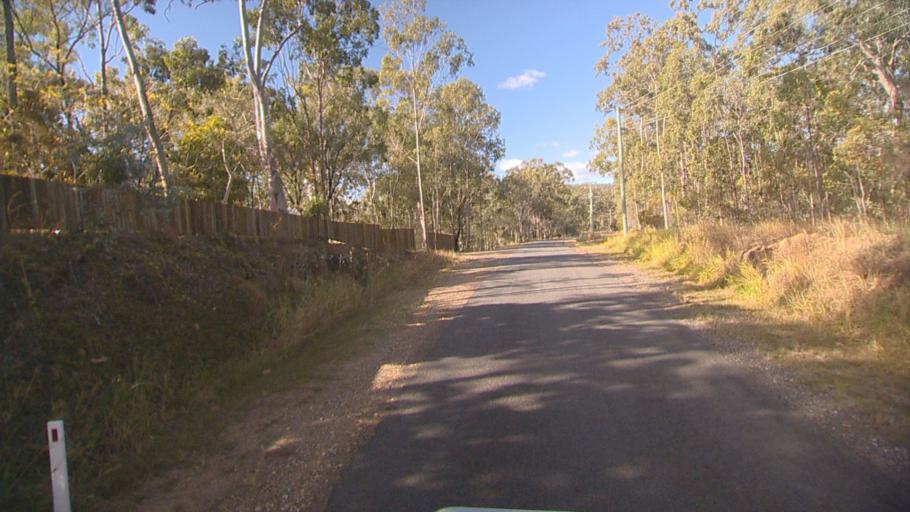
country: AU
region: Queensland
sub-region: Logan
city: Chambers Flat
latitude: -27.8245
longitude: 153.0707
